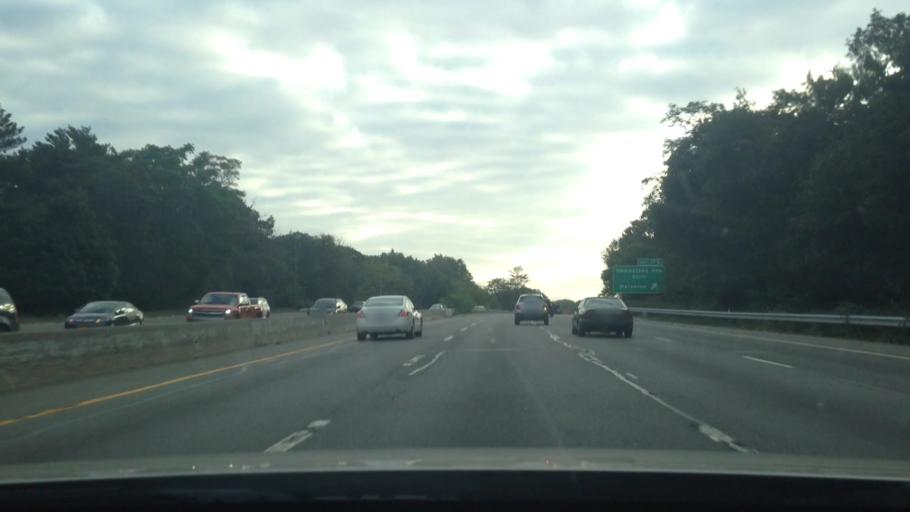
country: US
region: New York
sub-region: Nassau County
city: Malverne
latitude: 40.6829
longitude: -73.6696
